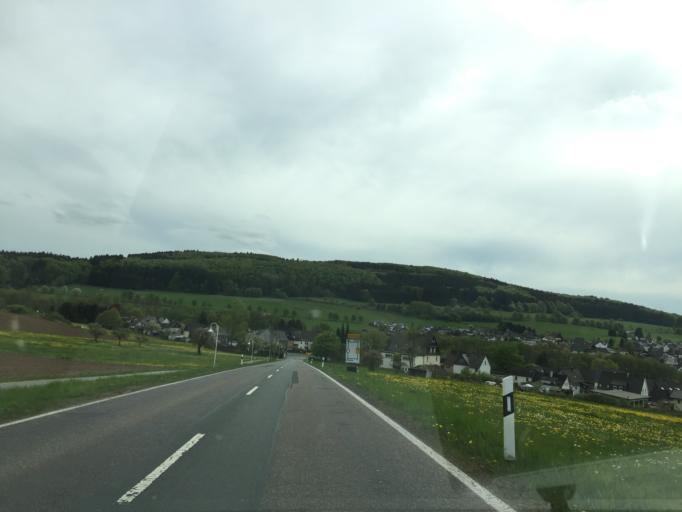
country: DE
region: Rheinland-Pfalz
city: Langenbach bei Marienberg
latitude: 50.6391
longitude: 7.9494
